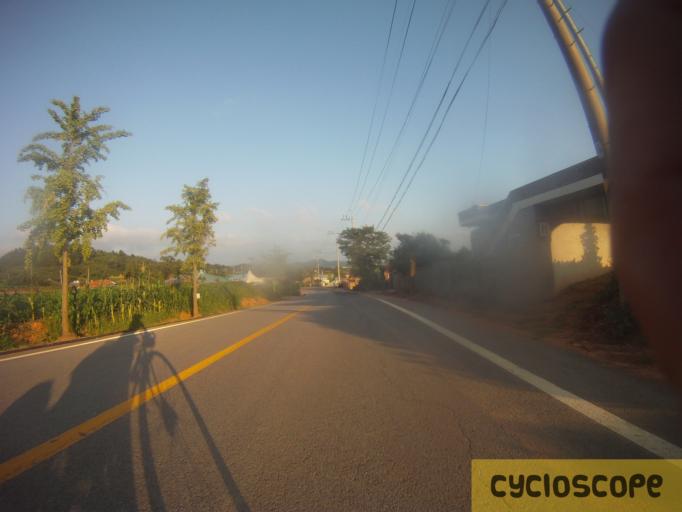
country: KR
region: Jeollanam-do
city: Reiko
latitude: 35.1463
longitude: 126.4137
